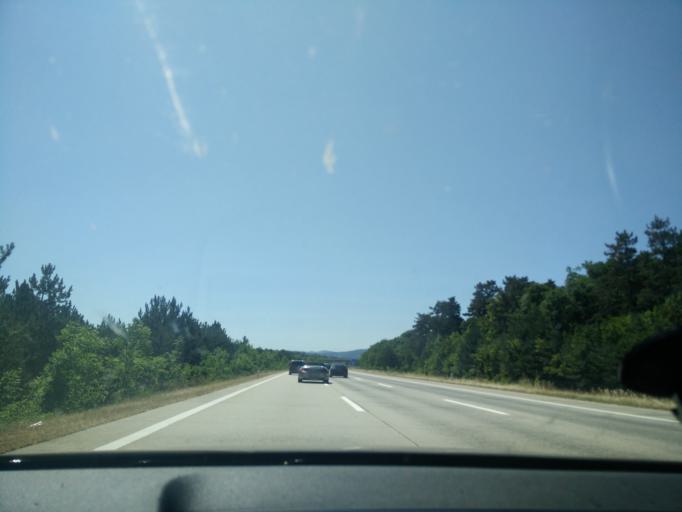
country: AT
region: Lower Austria
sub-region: Politischer Bezirk Wiener Neustadt
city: Bad Erlach
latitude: 47.7681
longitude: 16.2040
